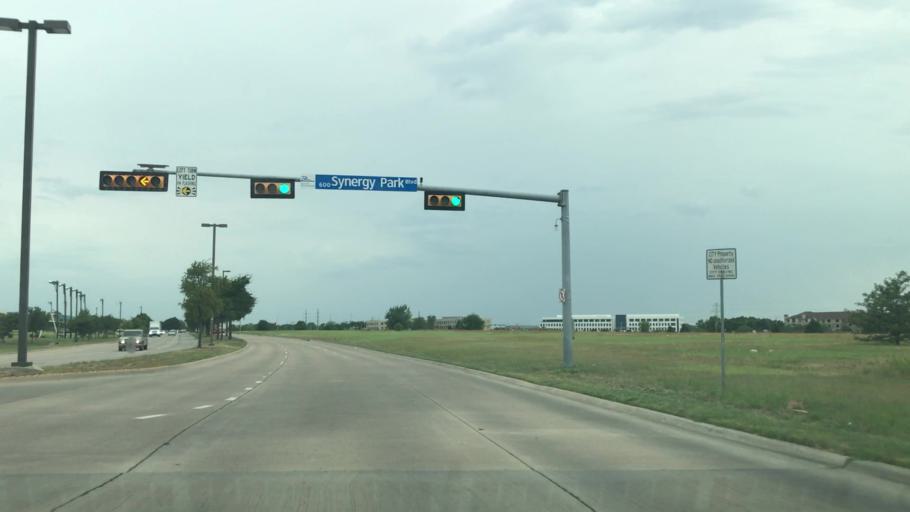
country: US
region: Texas
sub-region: Collin County
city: Plano
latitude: 33.0004
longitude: -96.7431
